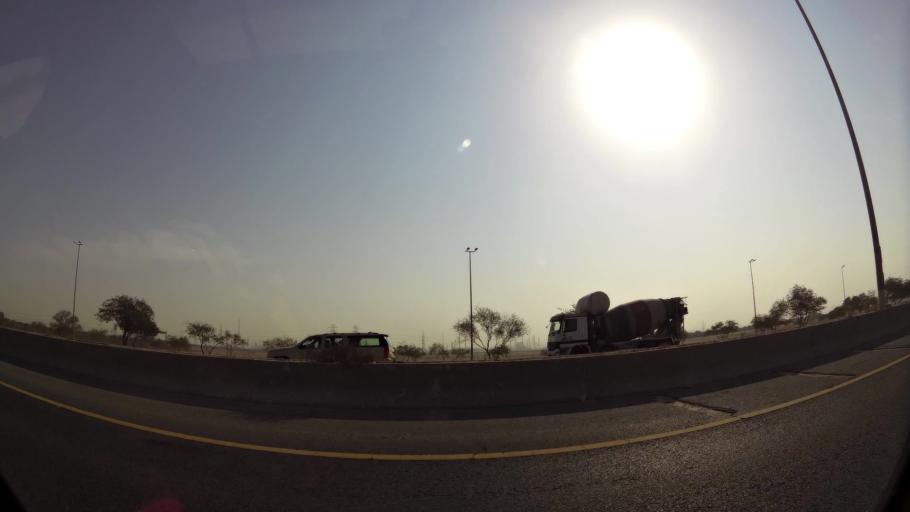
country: KW
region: Al Ahmadi
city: Al Ahmadi
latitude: 29.0554
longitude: 48.0965
